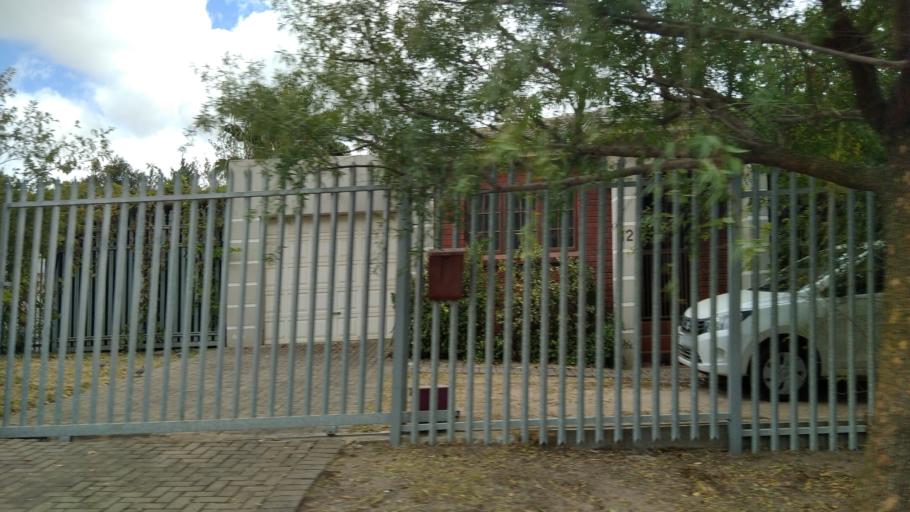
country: ZA
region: Western Cape
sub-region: City of Cape Town
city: Kraaifontein
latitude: -33.8222
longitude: 18.6828
